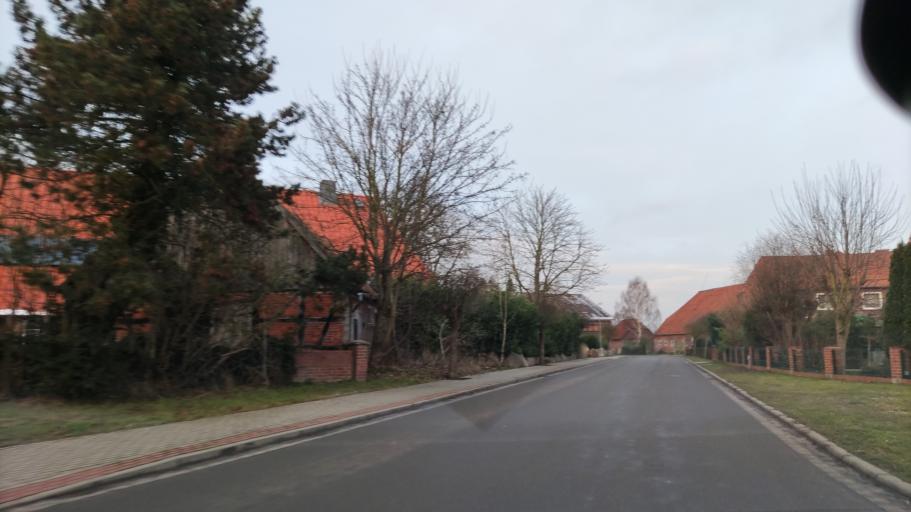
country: DE
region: Lower Saxony
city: Bleckede
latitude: 53.3142
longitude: 10.6746
